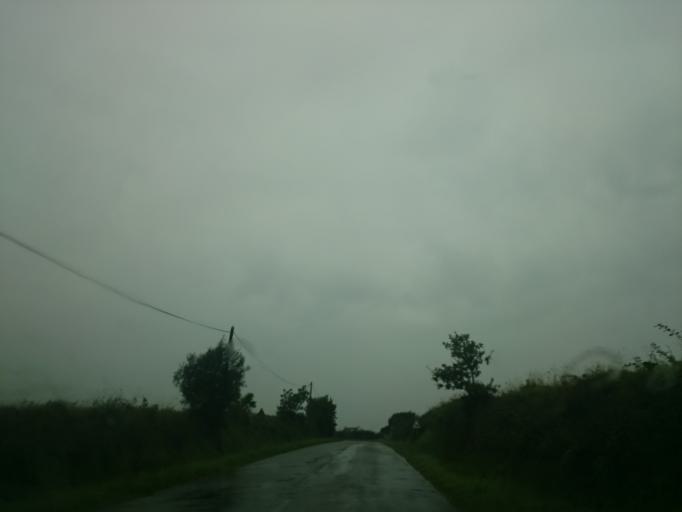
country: FR
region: Brittany
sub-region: Departement du Finistere
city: Le Drennec
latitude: 48.5373
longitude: -4.3760
